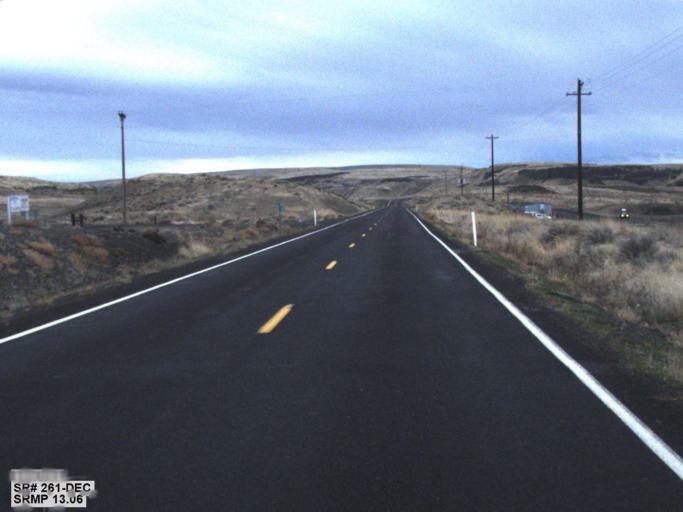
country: US
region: Washington
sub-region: Walla Walla County
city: Waitsburg
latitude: 46.5688
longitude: -118.1951
